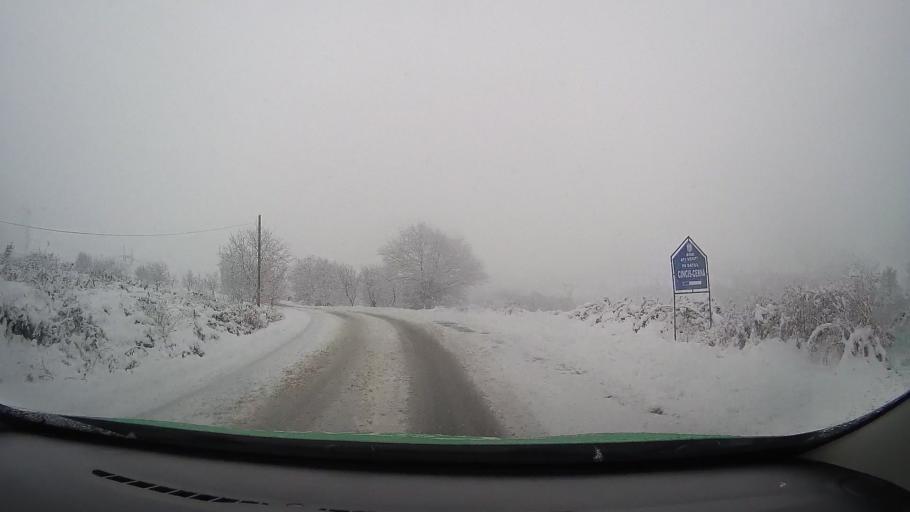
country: RO
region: Hunedoara
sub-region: Comuna Teliucu Inferior
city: Teliucu Inferior
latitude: 45.7038
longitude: 22.8817
